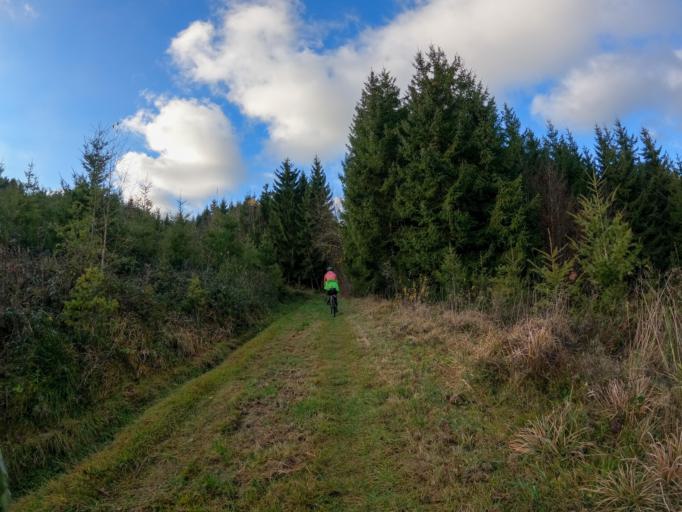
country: LU
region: Diekirch
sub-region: Canton de Wiltz
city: Winseler
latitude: 49.9892
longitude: 5.8505
